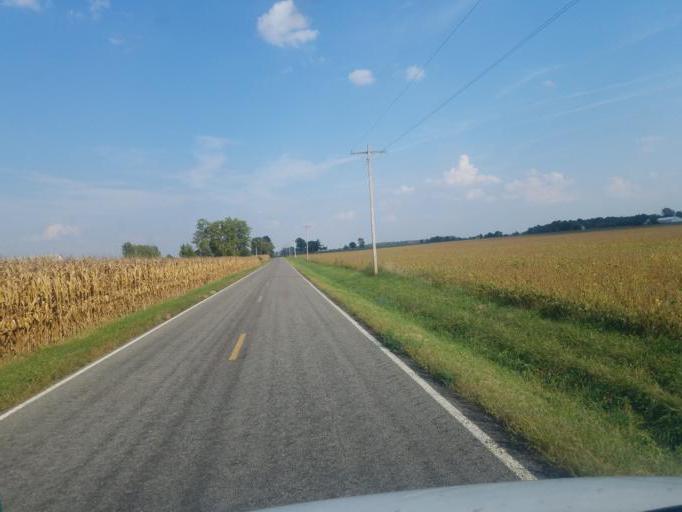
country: US
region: Ohio
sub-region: Hardin County
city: Forest
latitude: 40.9050
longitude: -83.5098
